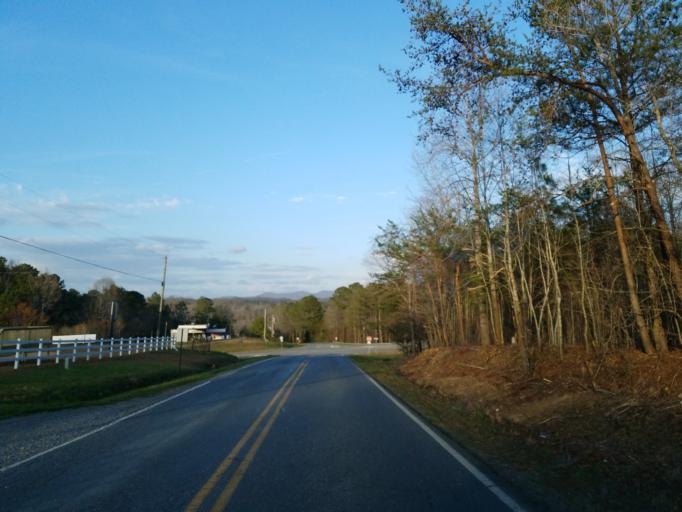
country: US
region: Georgia
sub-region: Pickens County
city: Jasper
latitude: 34.5067
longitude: -84.5168
